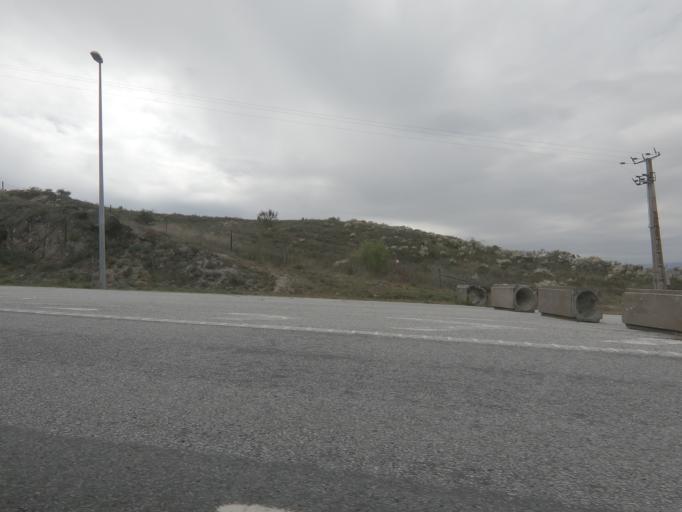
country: PT
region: Guarda
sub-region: Guarda
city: Guarda
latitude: 40.5888
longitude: -7.2752
